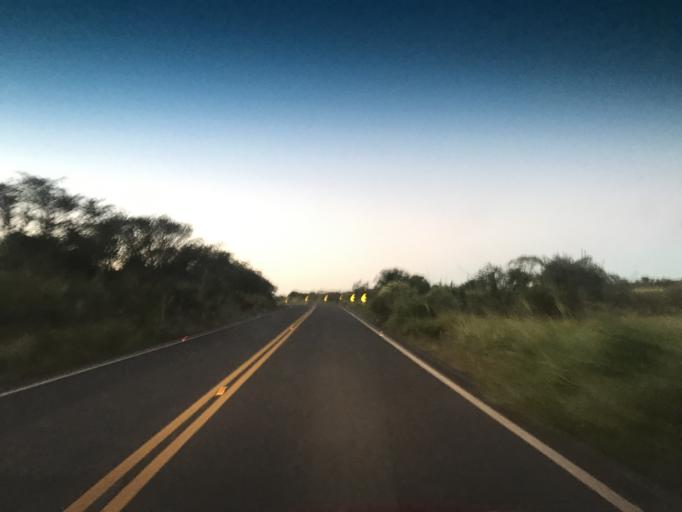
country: BR
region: Bahia
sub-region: Castro Alves
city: Castro Alves
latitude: -12.7515
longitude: -39.4064
